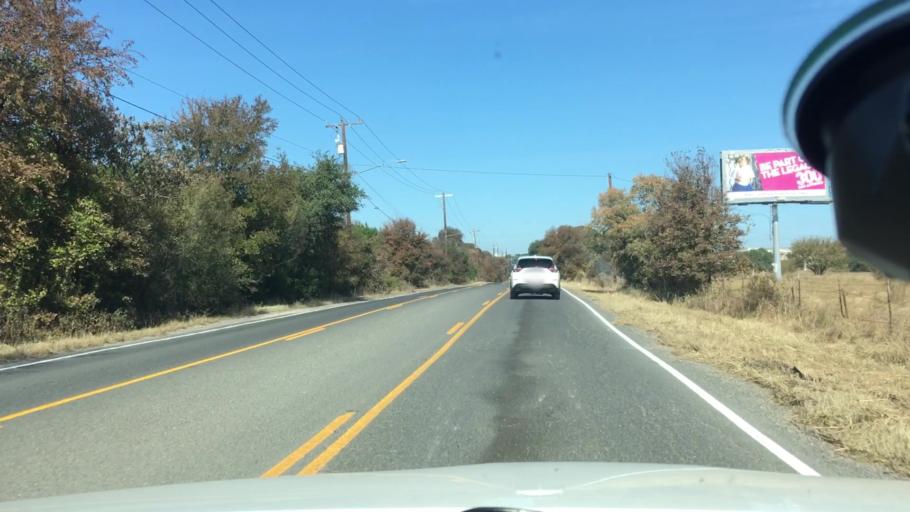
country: US
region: Texas
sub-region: Bexar County
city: Hollywood Park
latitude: 29.5891
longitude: -98.4237
